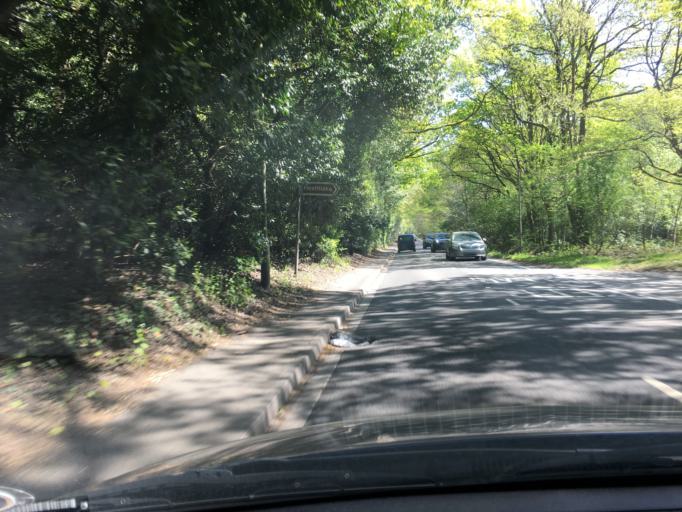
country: GB
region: England
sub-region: Bracknell Forest
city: Crowthorne
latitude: 51.3825
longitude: -0.8124
